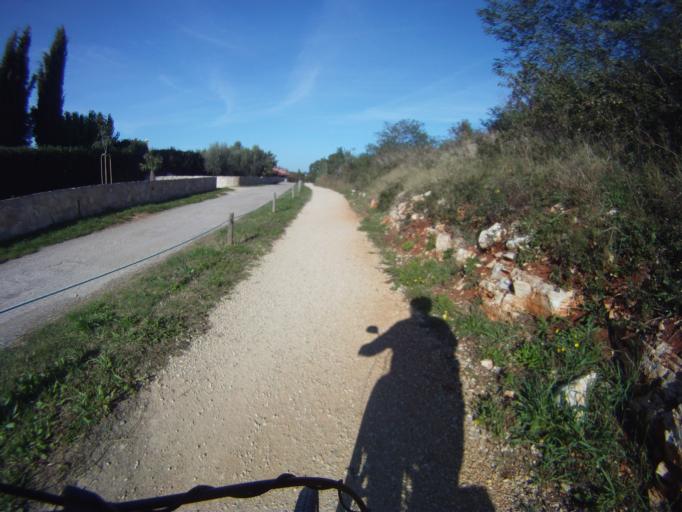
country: HR
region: Istarska
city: Novigrad
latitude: 45.3360
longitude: 13.5423
